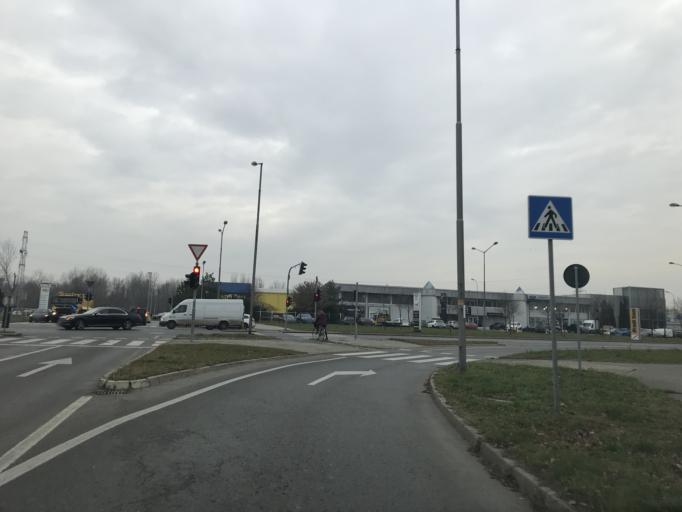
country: RS
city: Veternik
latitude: 45.2549
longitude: 19.7947
